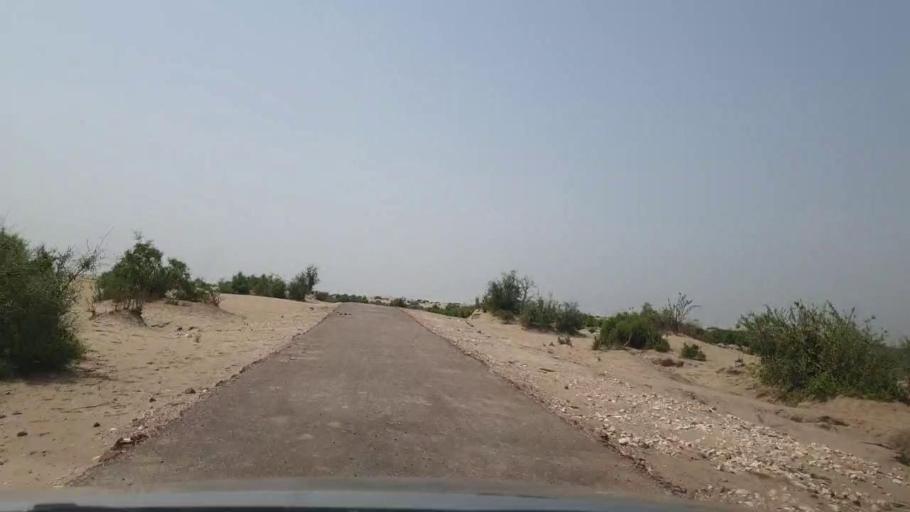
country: PK
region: Sindh
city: Pano Aqil
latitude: 27.6066
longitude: 69.1468
